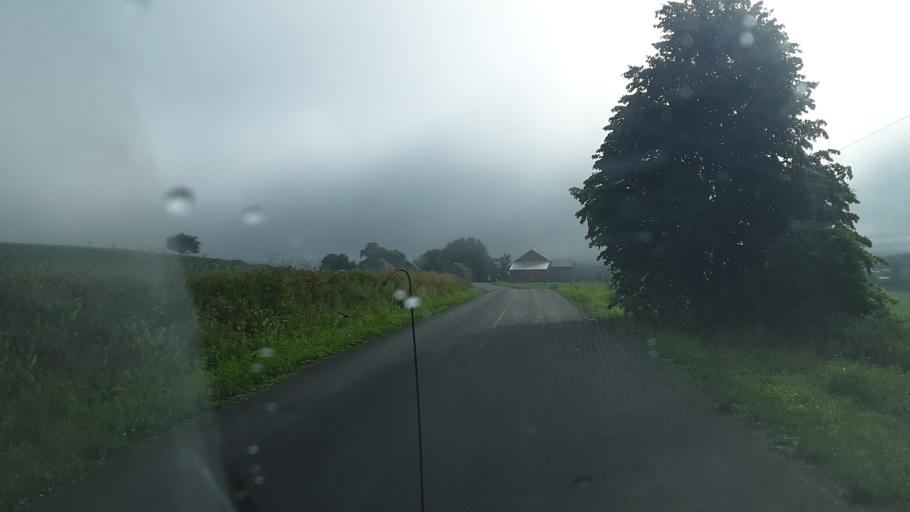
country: US
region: New York
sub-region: Montgomery County
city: Fonda
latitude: 42.9072
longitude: -74.3802
